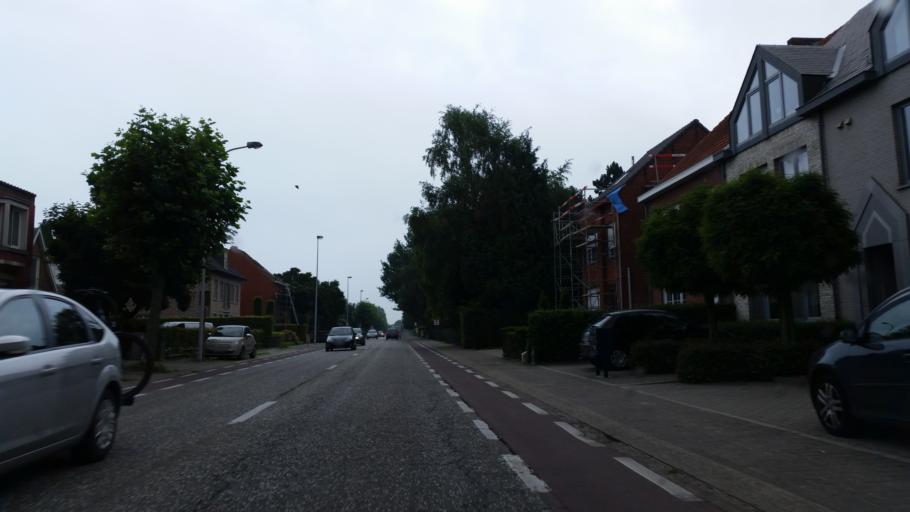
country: BE
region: Flanders
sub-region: Provincie Antwerpen
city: Hoogstraten
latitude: 51.4114
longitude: 4.7634
